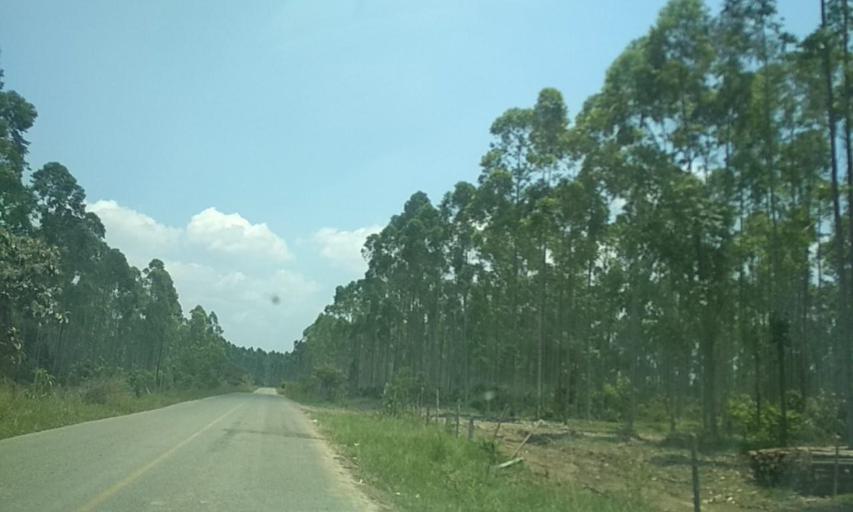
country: MX
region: Tabasco
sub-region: Huimanguillo
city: Francisco Rueda
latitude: 17.8411
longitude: -93.8869
